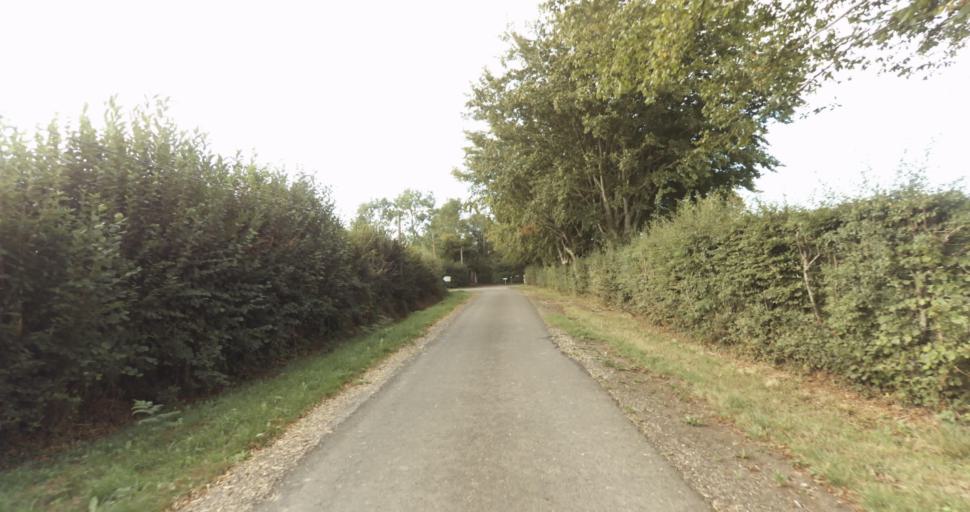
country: FR
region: Lower Normandy
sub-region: Departement de l'Orne
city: Gace
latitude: 48.8282
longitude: 0.2116
